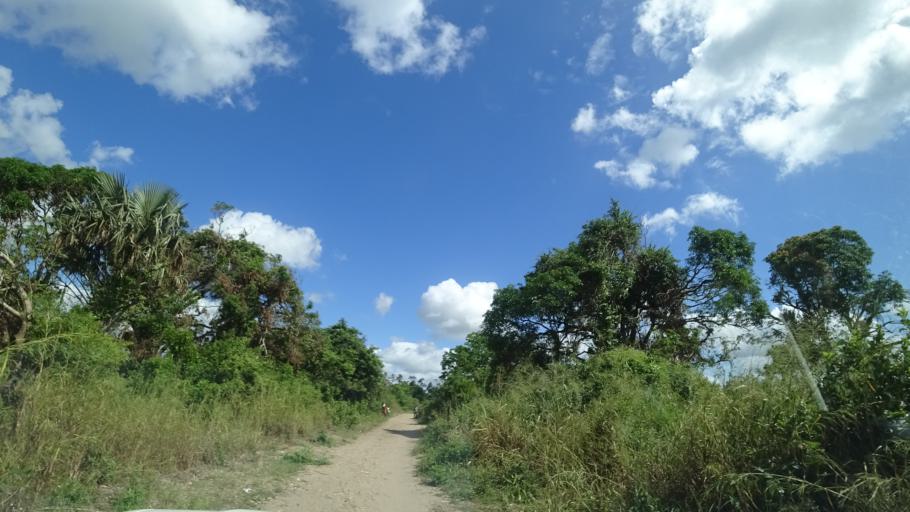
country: MZ
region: Sofala
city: Dondo
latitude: -19.3600
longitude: 34.5748
